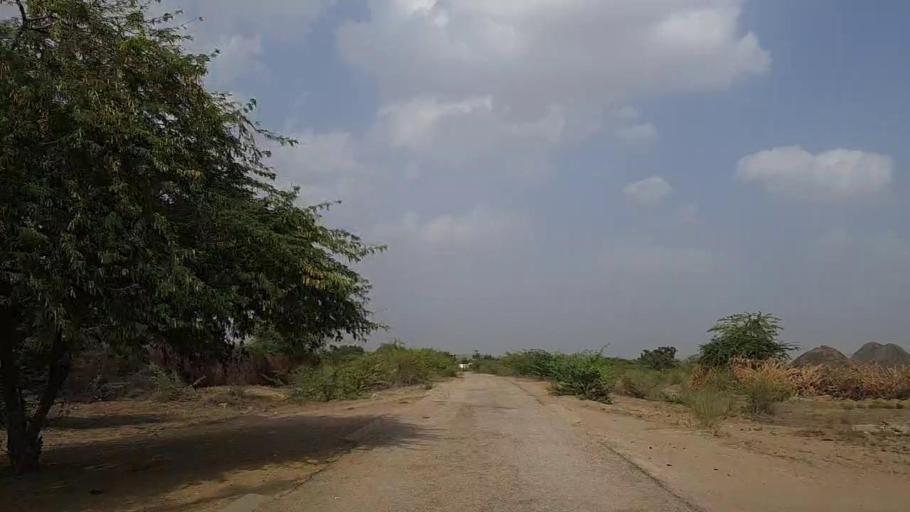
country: PK
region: Sindh
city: Islamkot
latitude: 24.8646
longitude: 70.1097
